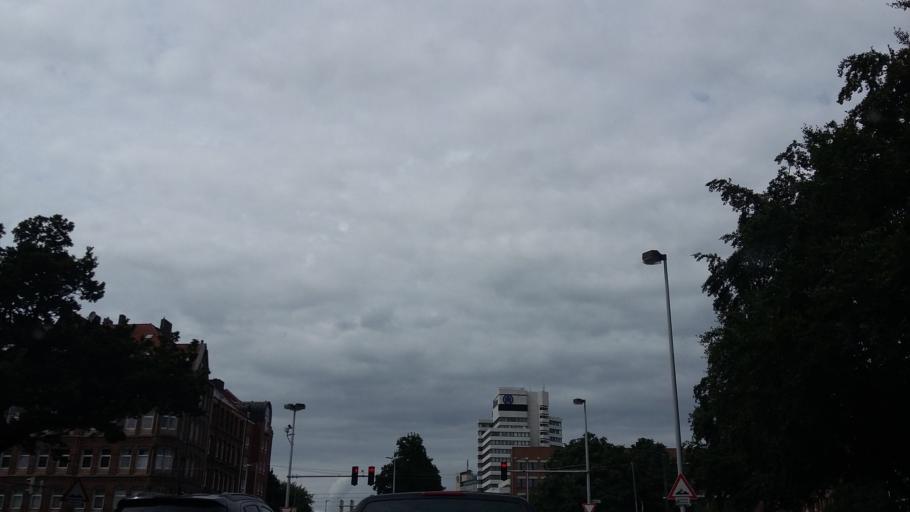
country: DE
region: Lower Saxony
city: Hannover
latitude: 52.3737
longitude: 9.7288
